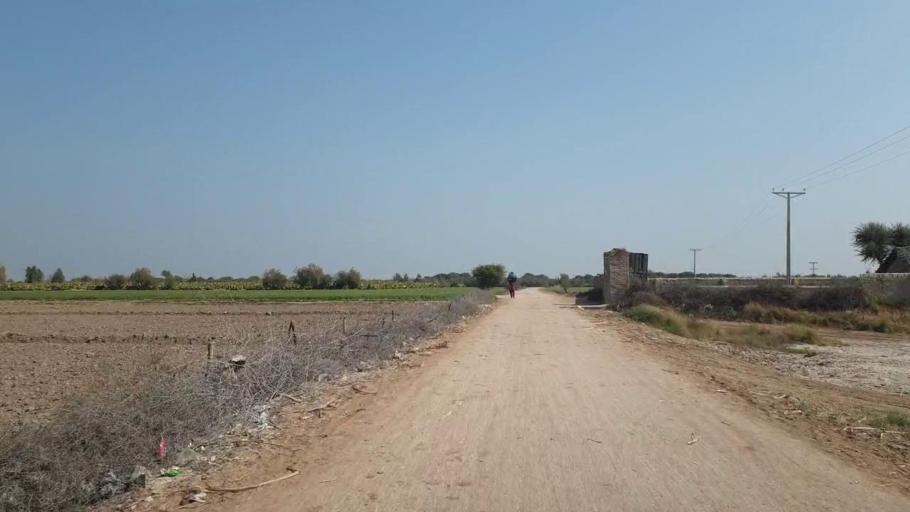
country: PK
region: Sindh
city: Hala
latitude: 25.9496
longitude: 68.4693
